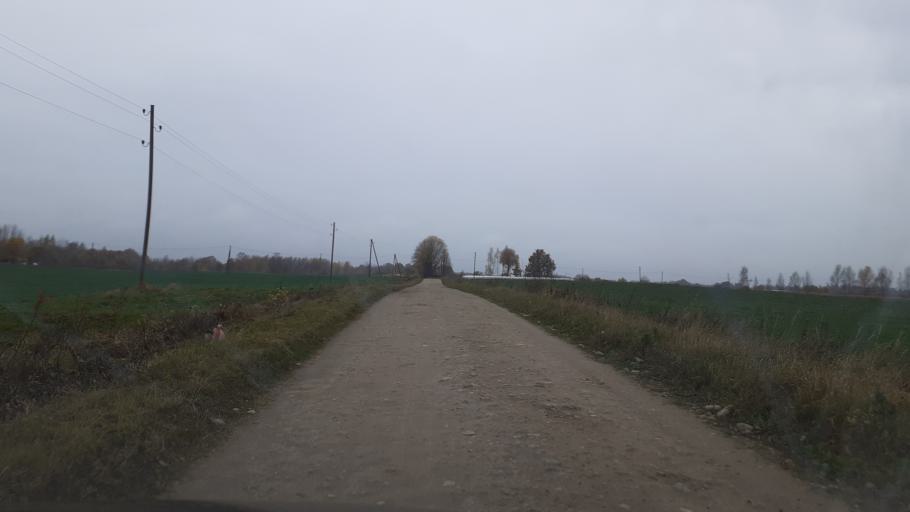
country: LV
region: Saldus Rajons
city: Saldus
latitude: 56.8637
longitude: 22.3500
